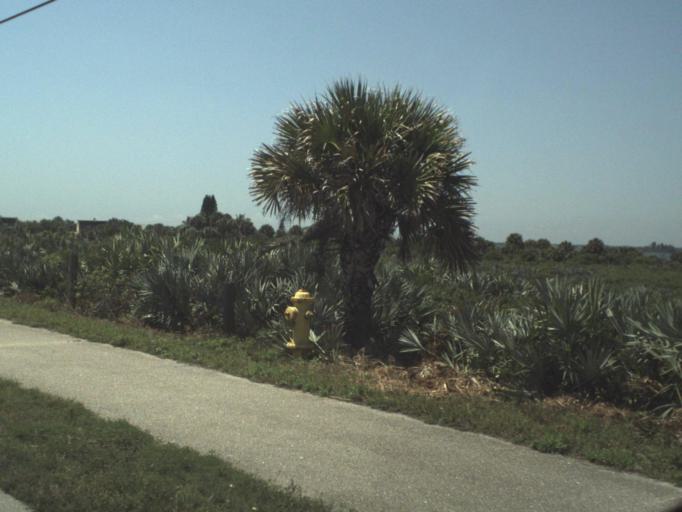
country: US
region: Florida
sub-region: Brevard County
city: Malabar
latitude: 28.0080
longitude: -80.5293
